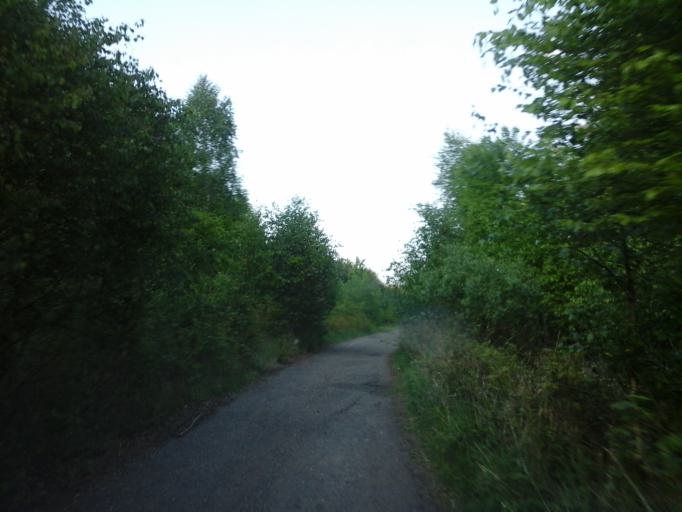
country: PL
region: West Pomeranian Voivodeship
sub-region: Powiat choszczenski
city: Krzecin
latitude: 53.0025
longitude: 15.5052
